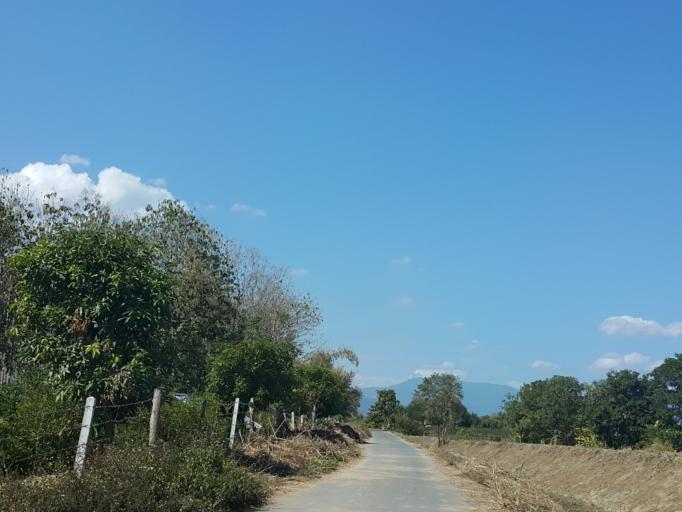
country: TH
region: Chiang Mai
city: Mae Taeng
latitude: 19.0979
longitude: 98.9400
